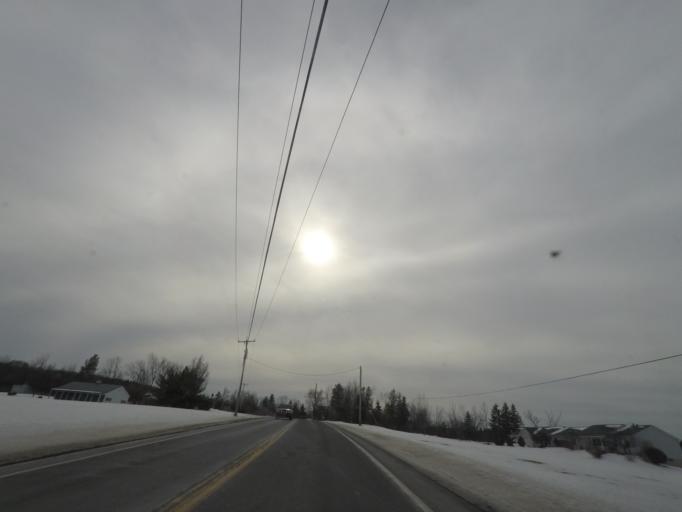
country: US
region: New York
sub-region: Albany County
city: Altamont
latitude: 42.6888
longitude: -74.0686
